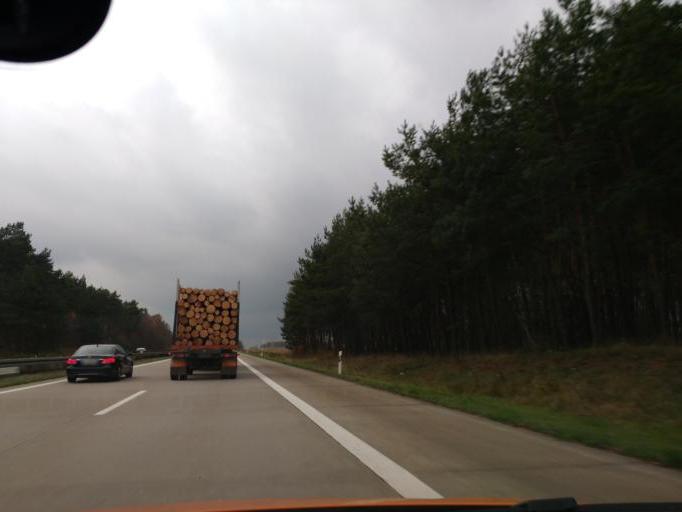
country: DE
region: Brandenburg
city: Heiligengrabe
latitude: 53.1711
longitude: 12.3423
